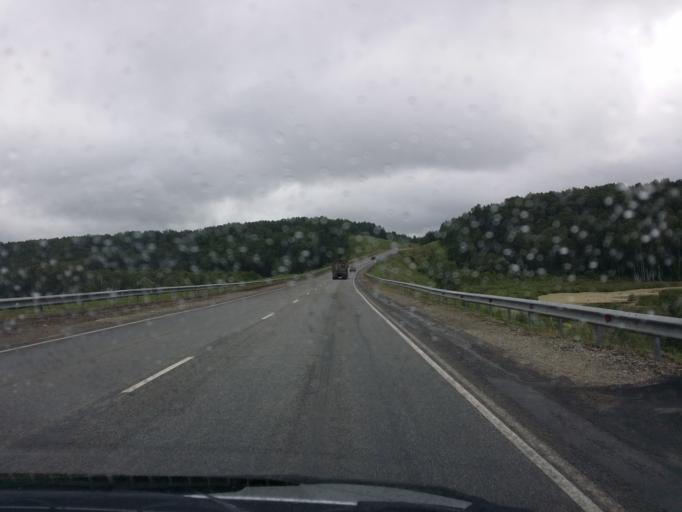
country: RU
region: Altai Krai
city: Nalobikha
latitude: 53.1545
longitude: 84.6909
